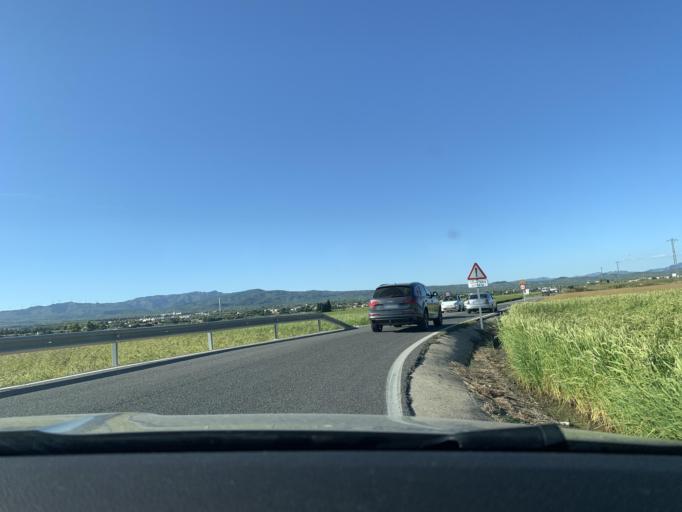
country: ES
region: Catalonia
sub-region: Provincia de Tarragona
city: Camarles
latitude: 40.7763
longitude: 0.6892
